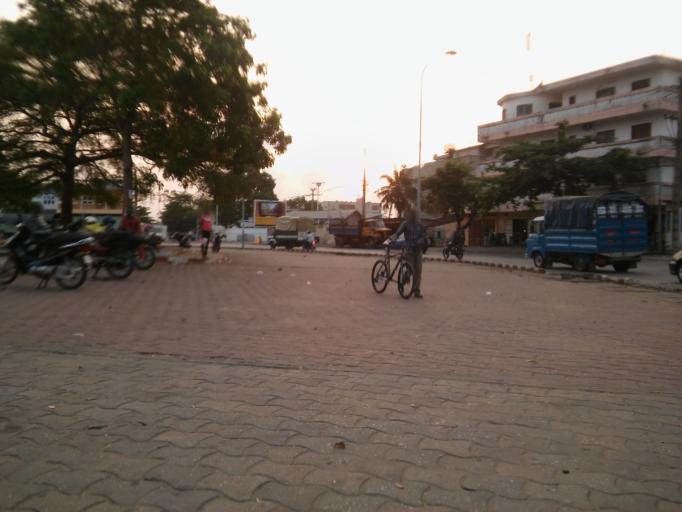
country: BJ
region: Littoral
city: Cotonou
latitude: 6.3702
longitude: 2.4469
